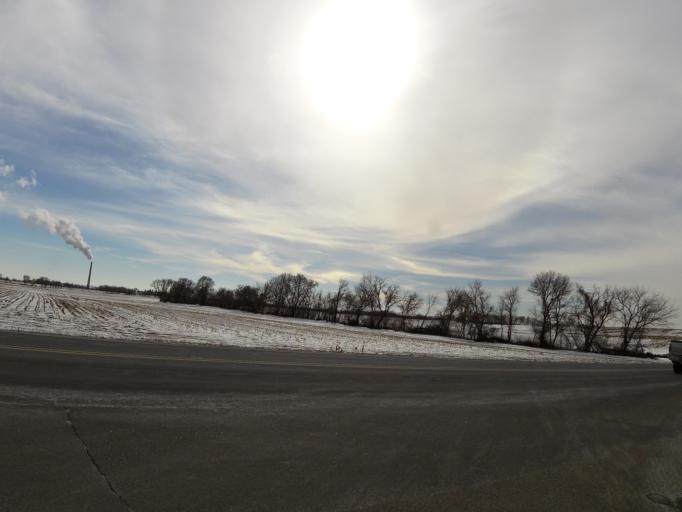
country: US
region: Minnesota
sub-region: Washington County
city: Stillwater
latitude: 45.0608
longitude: -92.7752
